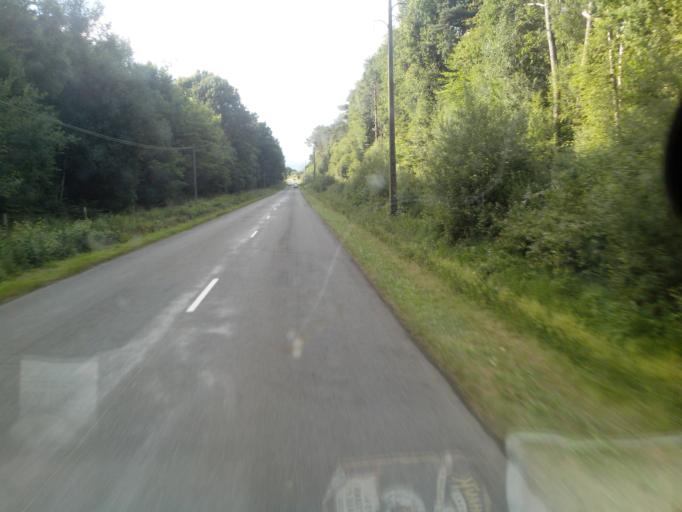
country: FR
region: Brittany
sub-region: Departement d'Ille-et-Vilaine
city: Paimpont
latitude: 48.0329
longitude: -2.1779
